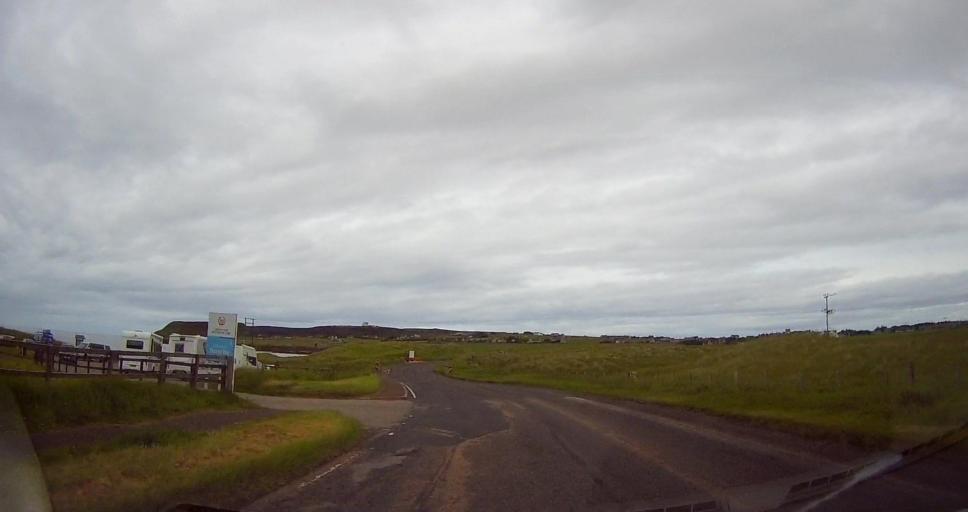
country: GB
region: Scotland
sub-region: Highland
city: Thurso
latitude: 58.6151
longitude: -3.3441
